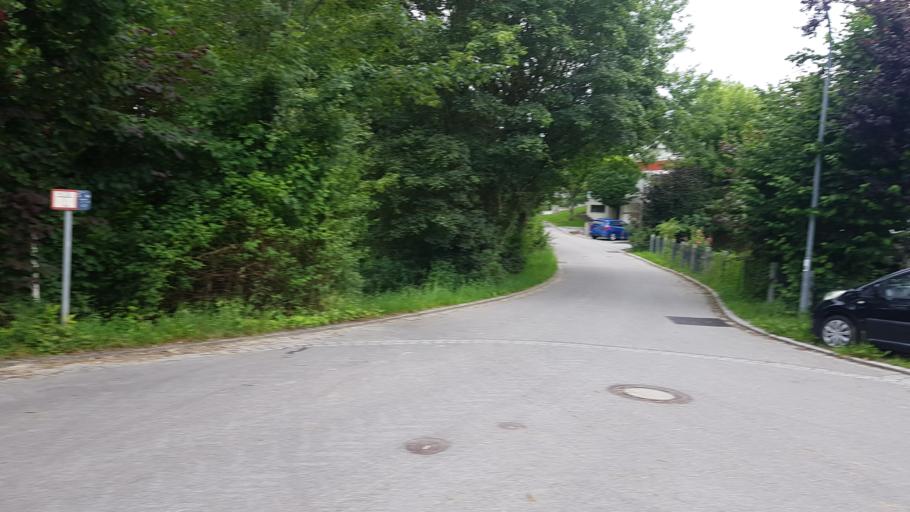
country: DE
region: Bavaria
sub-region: Upper Bavaria
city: Grafrath
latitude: 48.1301
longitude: 11.1659
